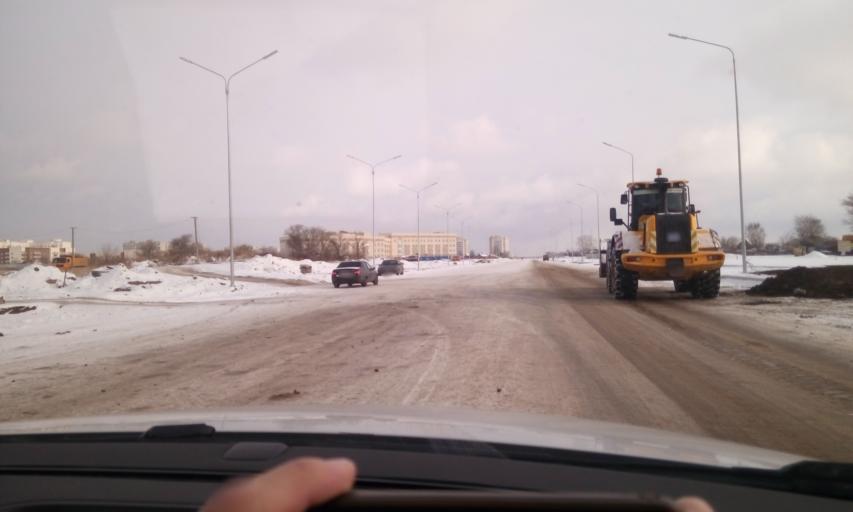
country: KZ
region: Astana Qalasy
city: Astana
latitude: 51.1215
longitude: 71.4892
